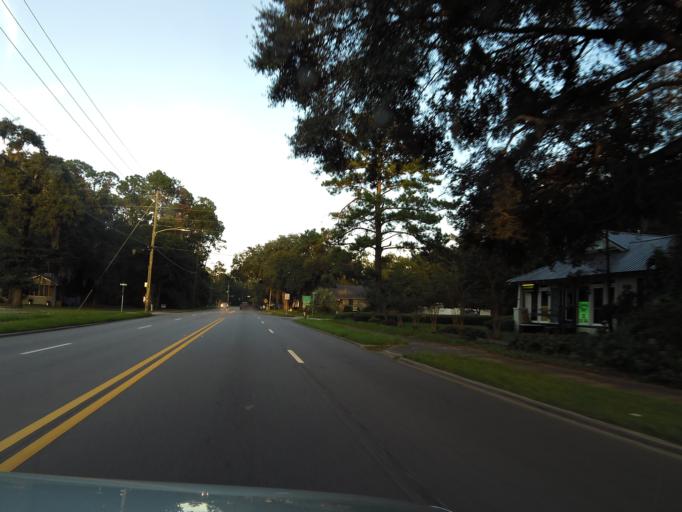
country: US
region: Georgia
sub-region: Camden County
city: Kingsland
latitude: 30.8006
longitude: -81.6868
